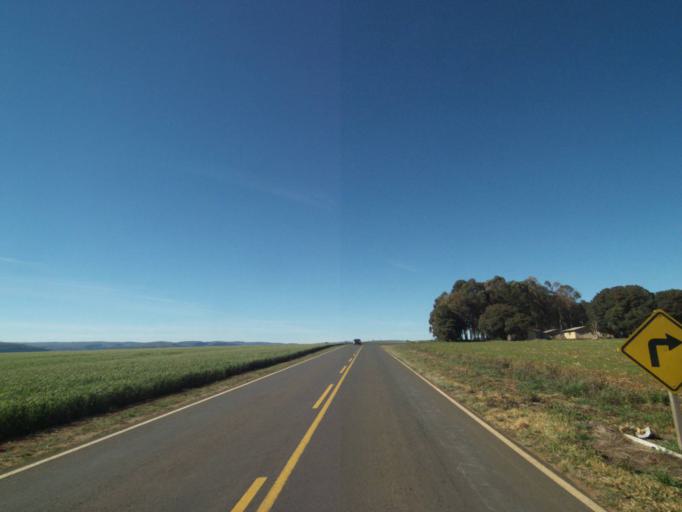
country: BR
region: Parana
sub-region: Tibagi
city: Tibagi
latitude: -24.5514
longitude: -50.2923
